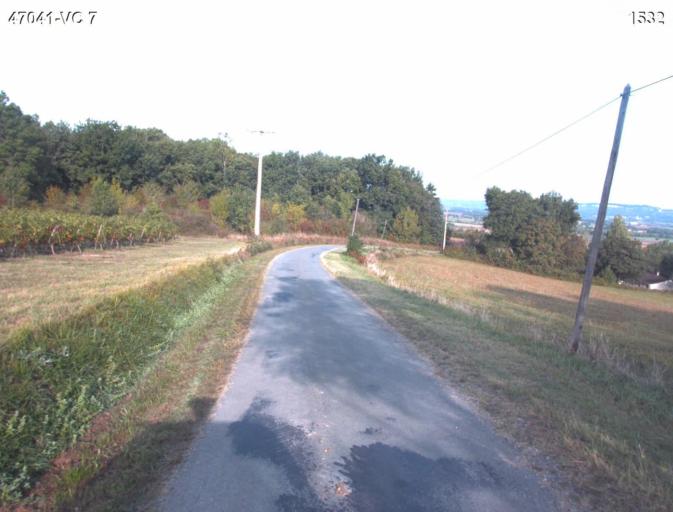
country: FR
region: Aquitaine
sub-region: Departement du Lot-et-Garonne
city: Port-Sainte-Marie
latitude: 44.1964
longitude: 0.4170
